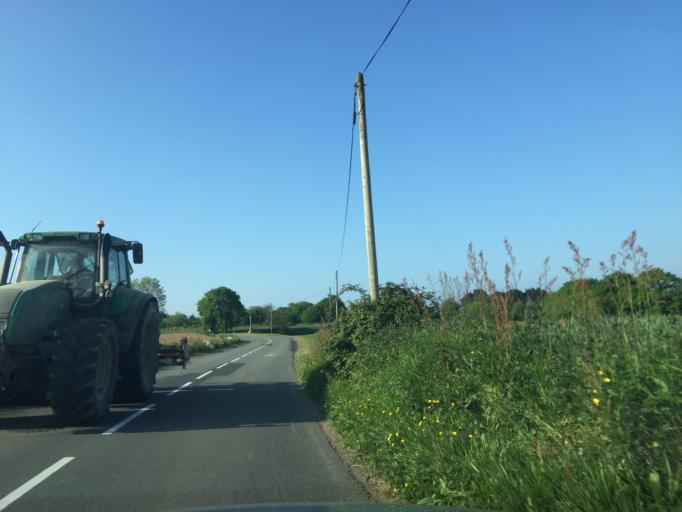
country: FR
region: Brittany
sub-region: Departement des Cotes-d'Armor
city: Saint-Cast-le-Guildo
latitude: 48.6047
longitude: -2.2537
